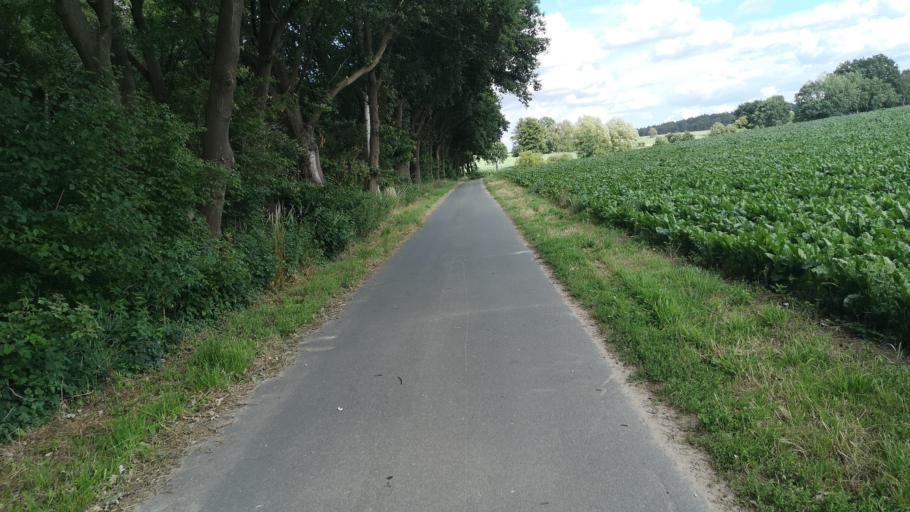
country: DE
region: Lower Saxony
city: Thomasburg
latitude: 53.2198
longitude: 10.6867
